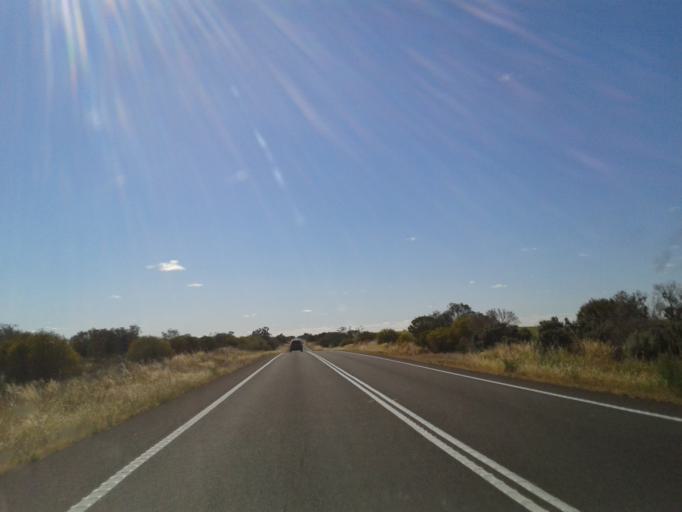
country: AU
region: South Australia
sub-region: Renmark Paringa
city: Renmark
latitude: -34.2745
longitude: 141.2095
